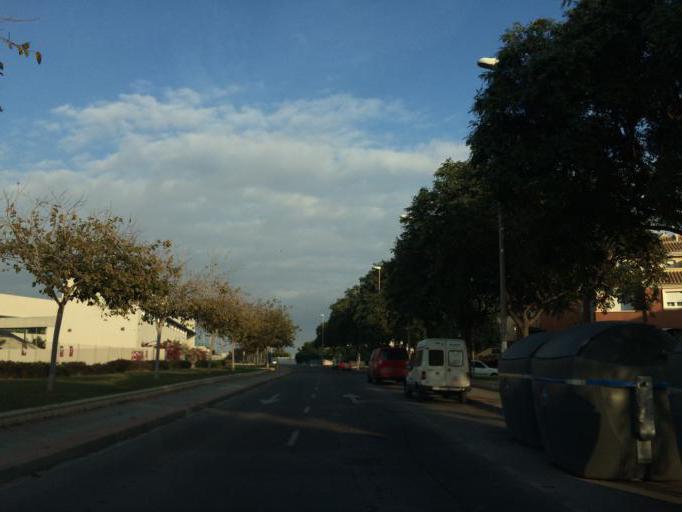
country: ES
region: Andalusia
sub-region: Provincia de Almeria
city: Almeria
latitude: 36.8246
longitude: -2.4378
